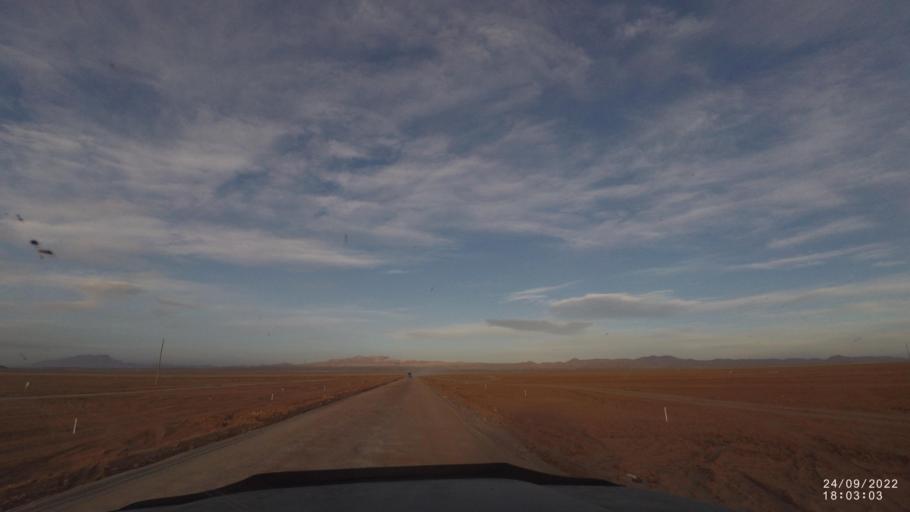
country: BO
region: Potosi
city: Colchani
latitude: -20.3099
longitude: -66.9718
